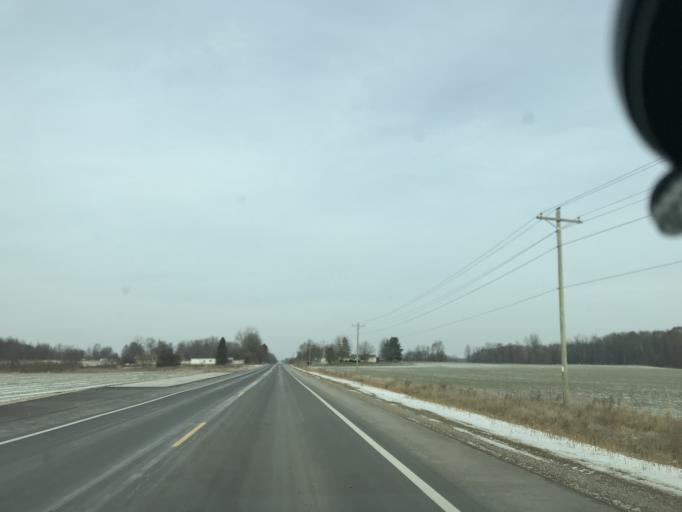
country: US
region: Michigan
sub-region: Ionia County
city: Lake Odessa
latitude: 42.7874
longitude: -85.0744
